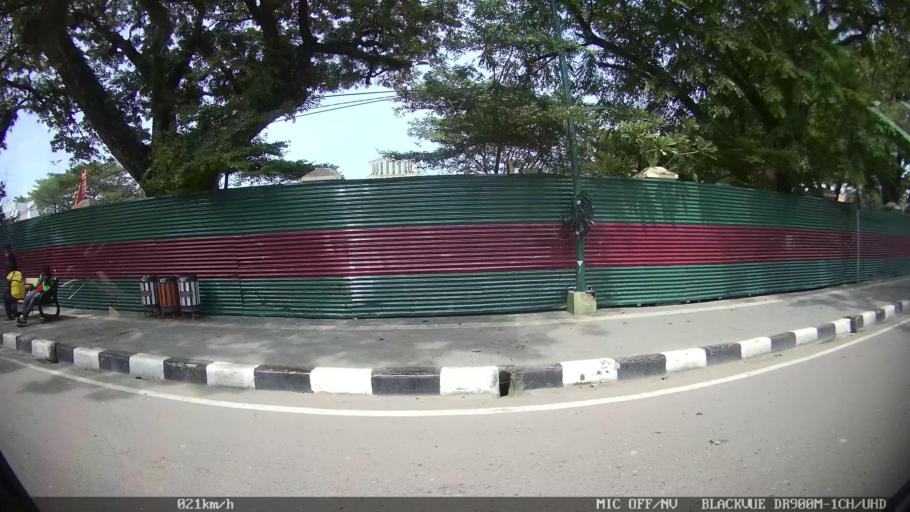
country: ID
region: North Sumatra
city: Medan
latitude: 3.5919
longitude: 98.6792
